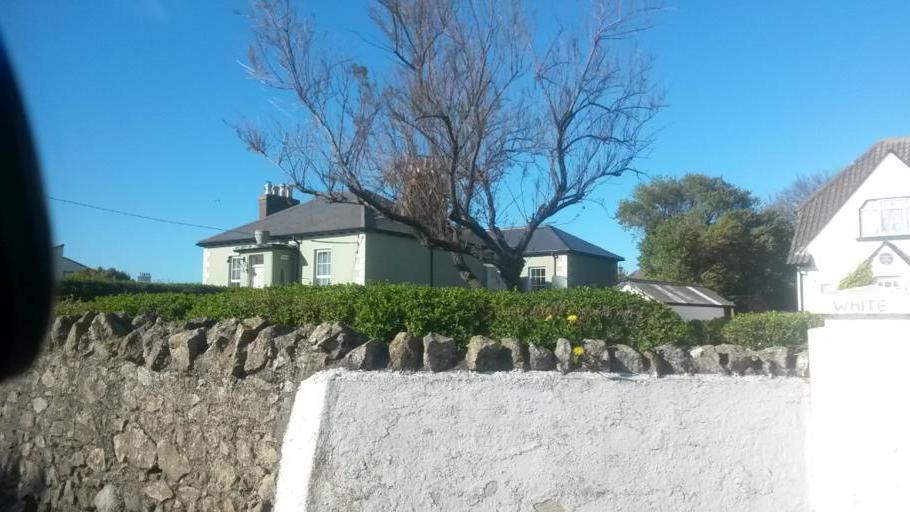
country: IE
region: Leinster
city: Sutton
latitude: 53.3766
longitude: -6.1014
